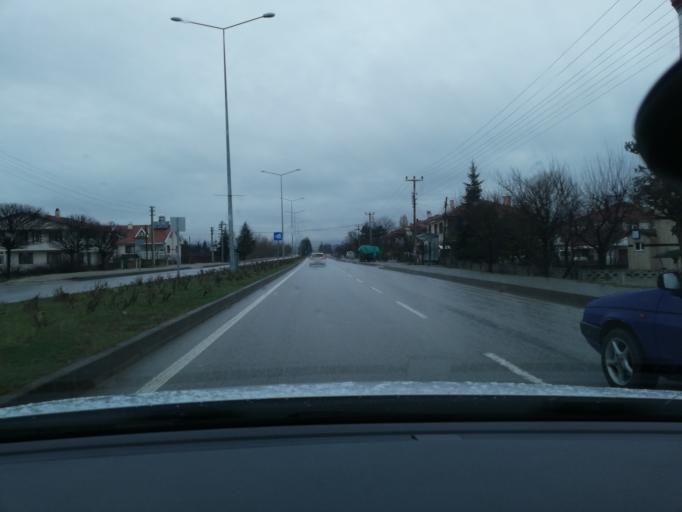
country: TR
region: Bolu
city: Bolu
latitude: 40.7065
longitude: 31.6173
